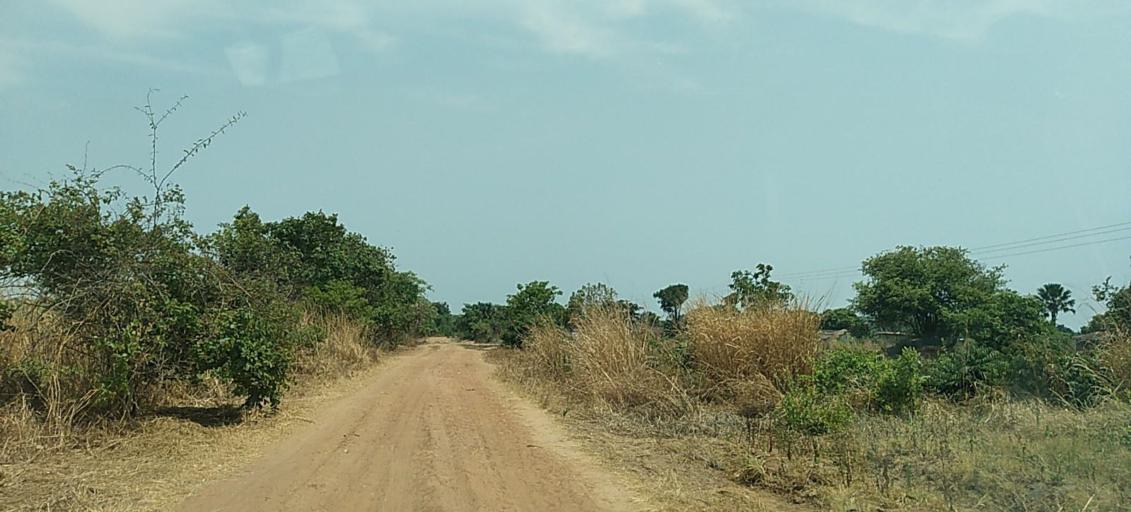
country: ZM
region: Copperbelt
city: Ndola
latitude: -13.0619
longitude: 28.7392
